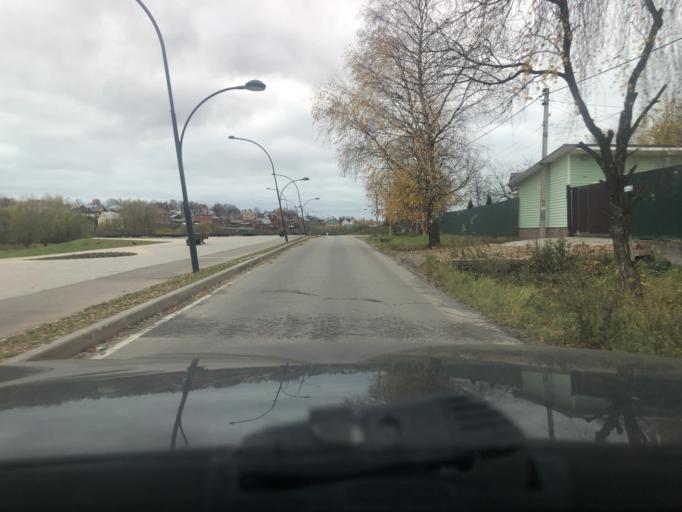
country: RU
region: Moskovskaya
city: Sergiyev Posad
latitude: 56.3027
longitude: 38.1175
